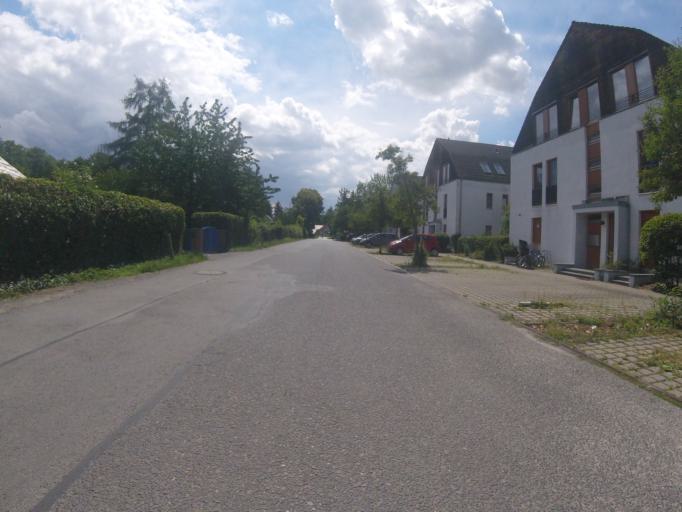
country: DE
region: Brandenburg
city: Bestensee
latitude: 52.2709
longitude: 13.6413
